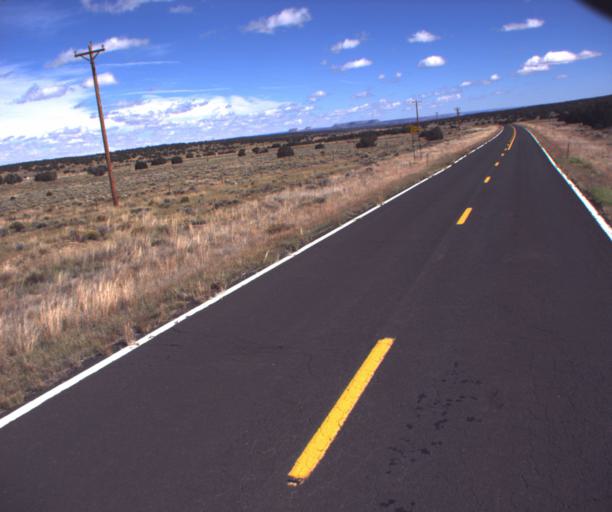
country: US
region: New Mexico
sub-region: McKinley County
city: Zuni Pueblo
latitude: 34.9909
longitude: -109.1068
